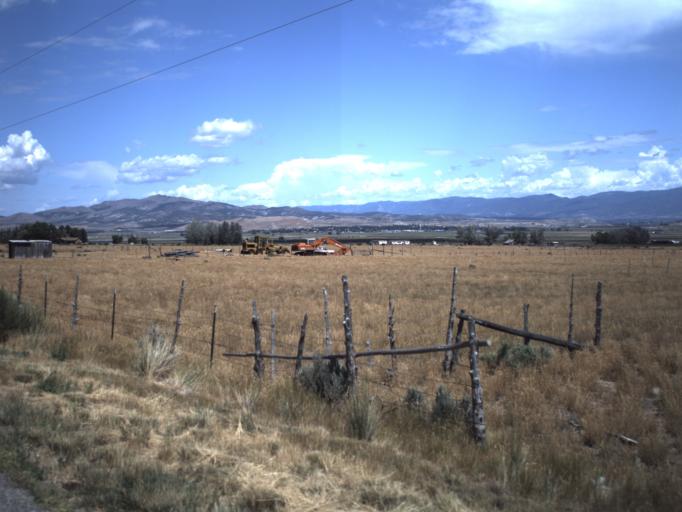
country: US
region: Utah
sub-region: Sanpete County
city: Moroni
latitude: 39.4779
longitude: -111.6350
